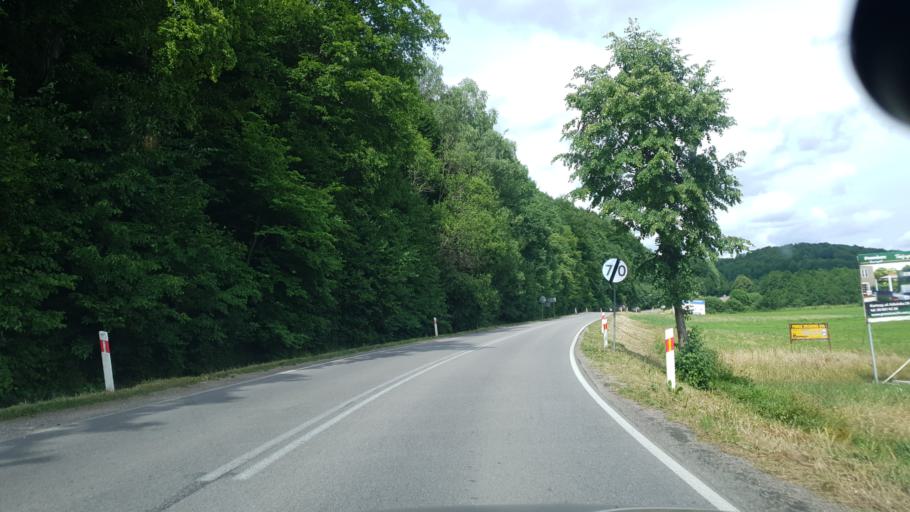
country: PL
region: Pomeranian Voivodeship
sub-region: Powiat kartuski
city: Kartuzy
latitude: 54.3091
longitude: 18.1504
